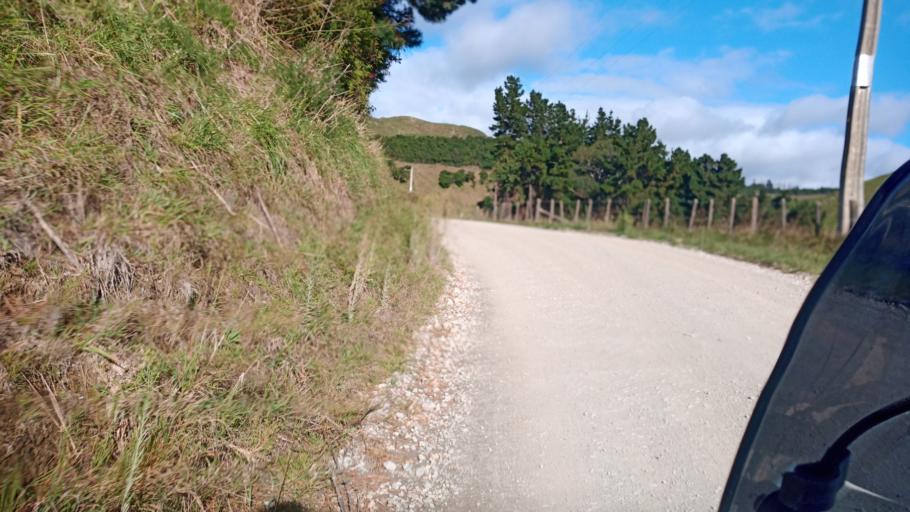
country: NZ
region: Gisborne
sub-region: Gisborne District
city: Gisborne
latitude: -38.5409
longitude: 177.5100
